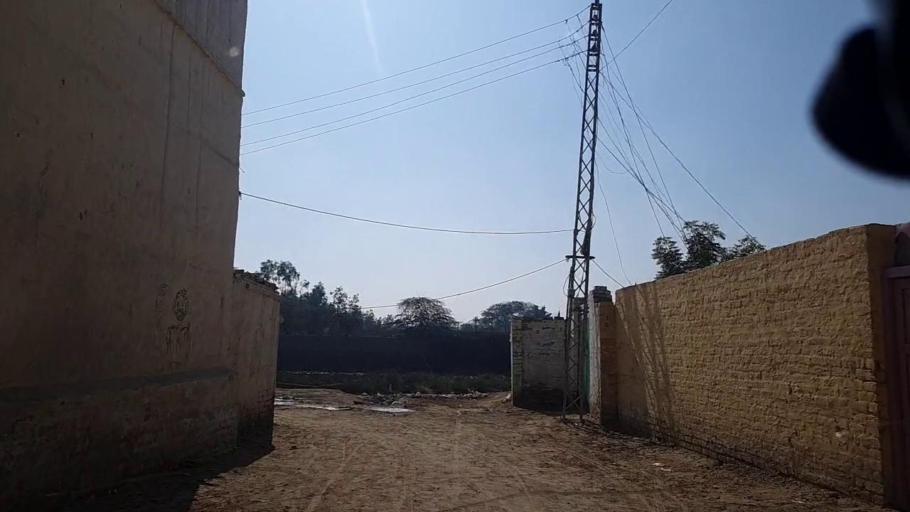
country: PK
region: Sindh
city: Khanpur
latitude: 27.8512
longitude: 69.4204
